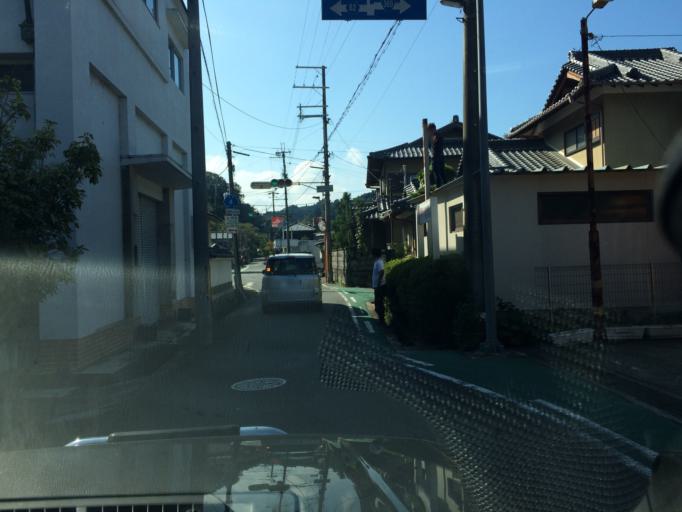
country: JP
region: Nara
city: Nara-shi
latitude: 34.7349
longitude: 135.9522
